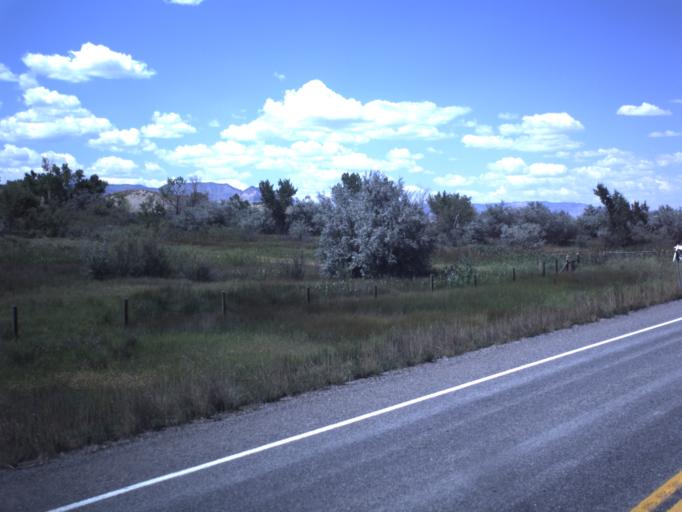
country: US
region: Utah
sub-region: Emery County
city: Castle Dale
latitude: 39.2141
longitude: -111.0001
